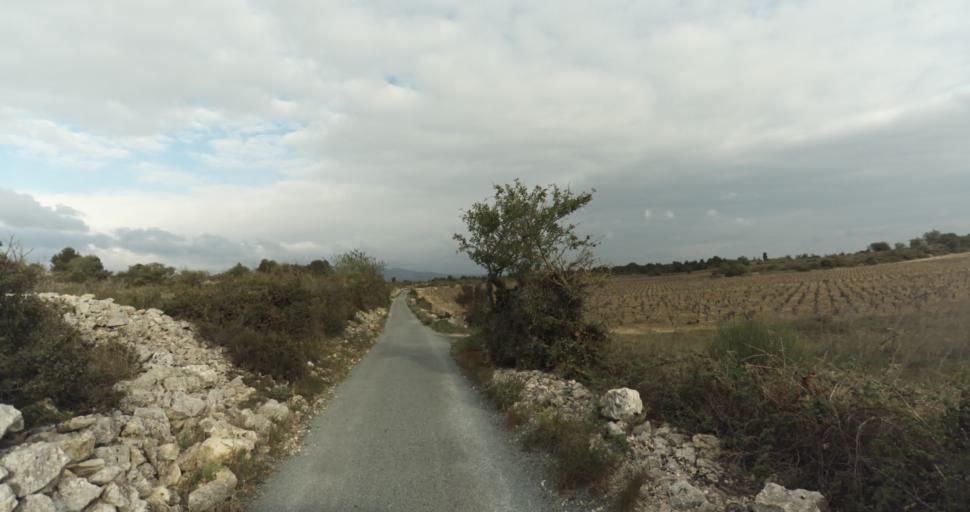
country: FR
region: Languedoc-Roussillon
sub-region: Departement de l'Aude
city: Leucate
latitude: 42.9263
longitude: 3.0273
